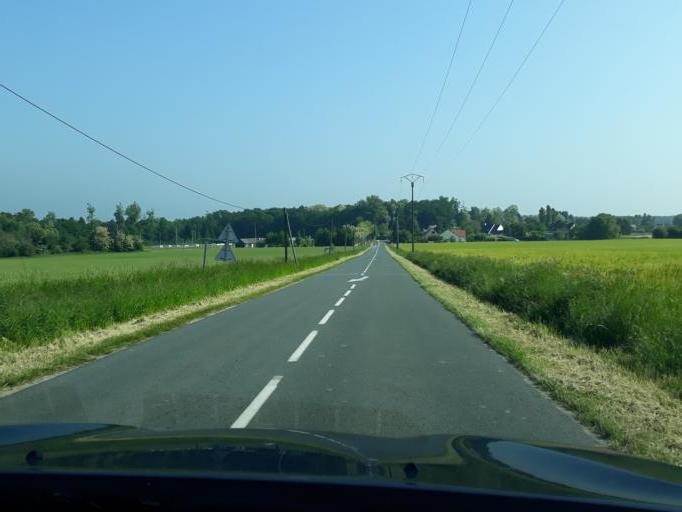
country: FR
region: Centre
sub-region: Departement du Loiret
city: Boigny-sur-Bionne
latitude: 47.9232
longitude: 2.0240
